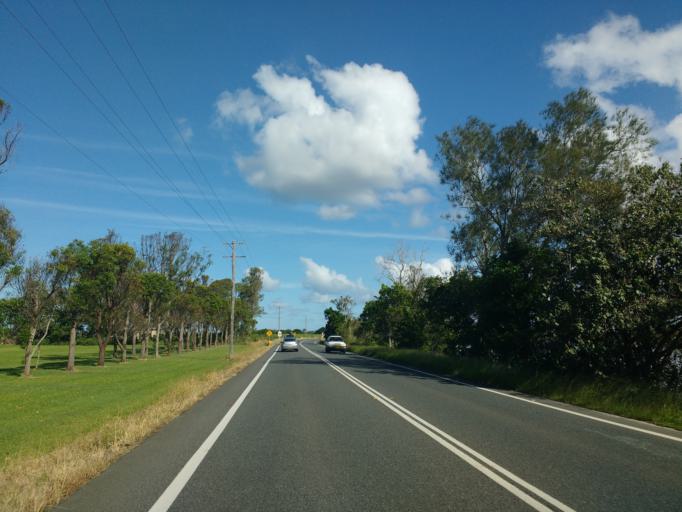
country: AU
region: New South Wales
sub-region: Richmond Valley
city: Evans Head
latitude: -28.9865
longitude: 153.4622
